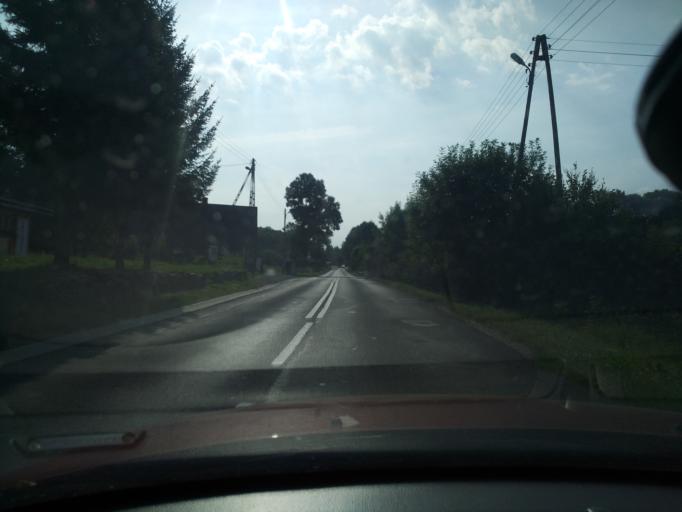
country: PL
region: Lower Silesian Voivodeship
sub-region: Powiat lwowecki
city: Lubomierz
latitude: 50.9734
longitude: 15.5007
